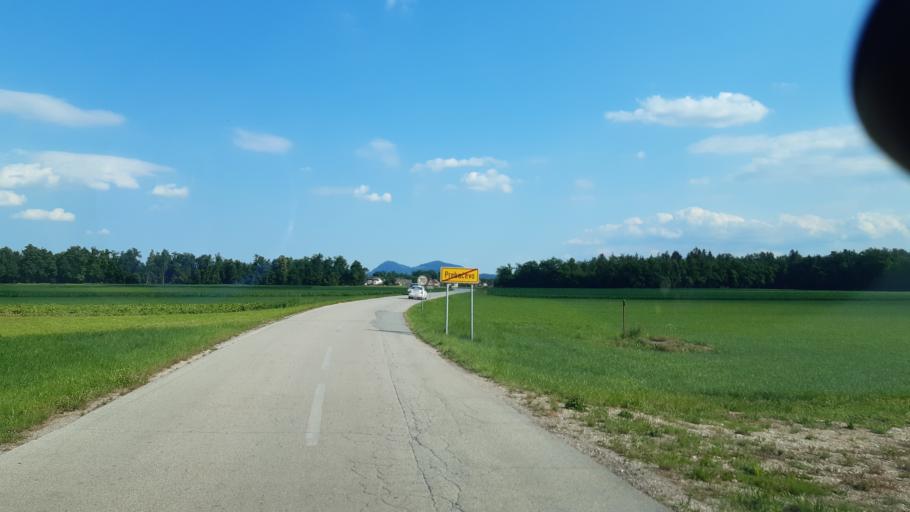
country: SI
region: Sencur
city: Hrastje
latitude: 46.2095
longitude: 14.3991
